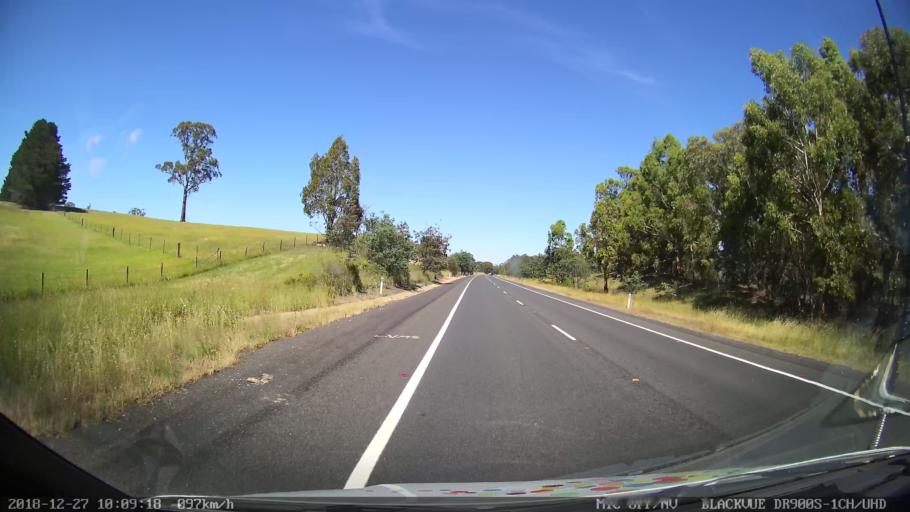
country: AU
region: New South Wales
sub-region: Lithgow
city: Portland
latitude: -33.4507
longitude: 149.8114
